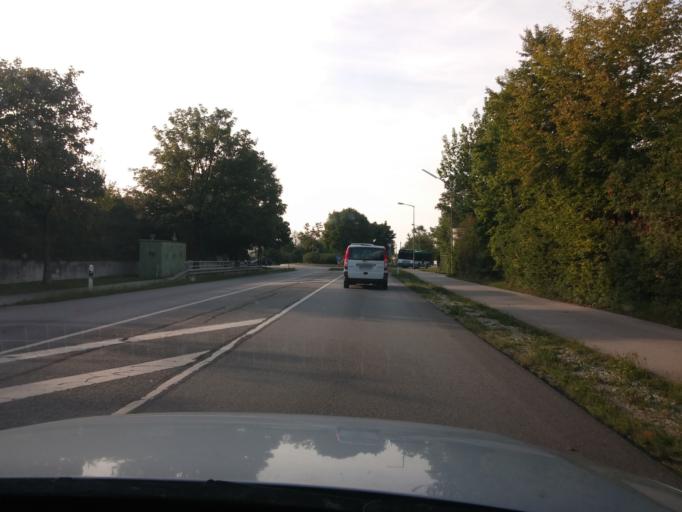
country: DE
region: Bavaria
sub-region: Upper Bavaria
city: Feldkirchen
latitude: 48.1530
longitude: 11.7256
